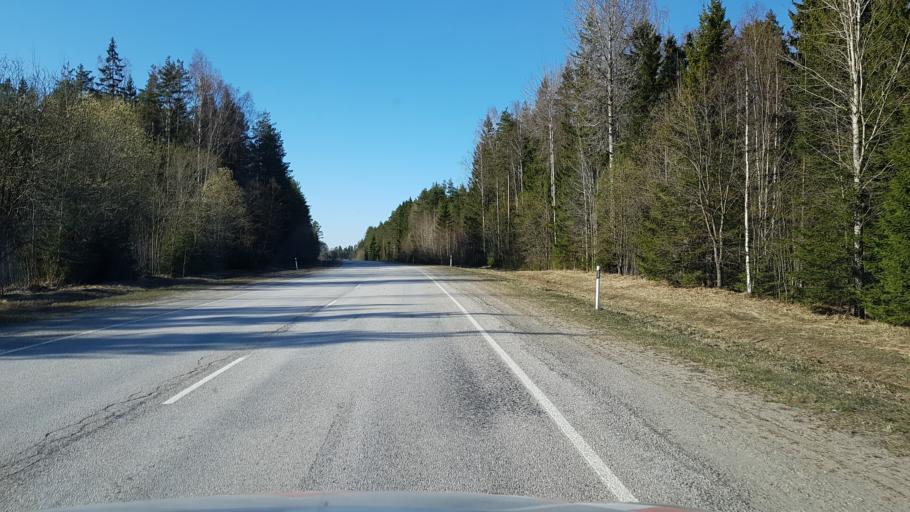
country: EE
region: Ida-Virumaa
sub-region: Johvi vald
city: Johvi
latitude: 59.1531
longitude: 27.3588
